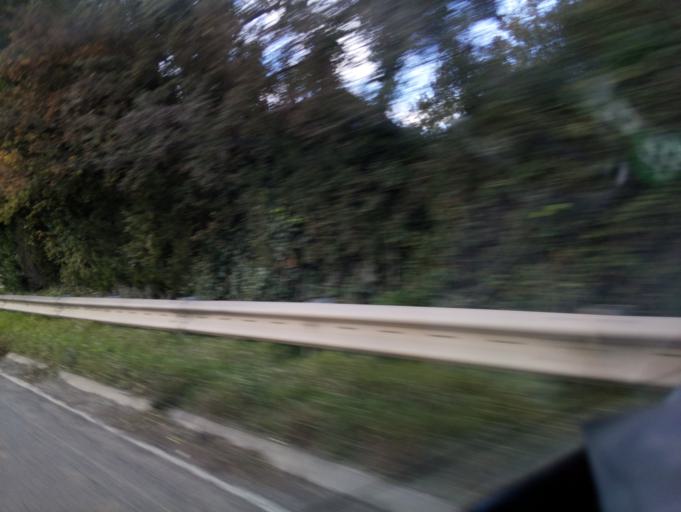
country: GB
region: England
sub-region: Herefordshire
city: Yatton
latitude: 52.0494
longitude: -2.5120
